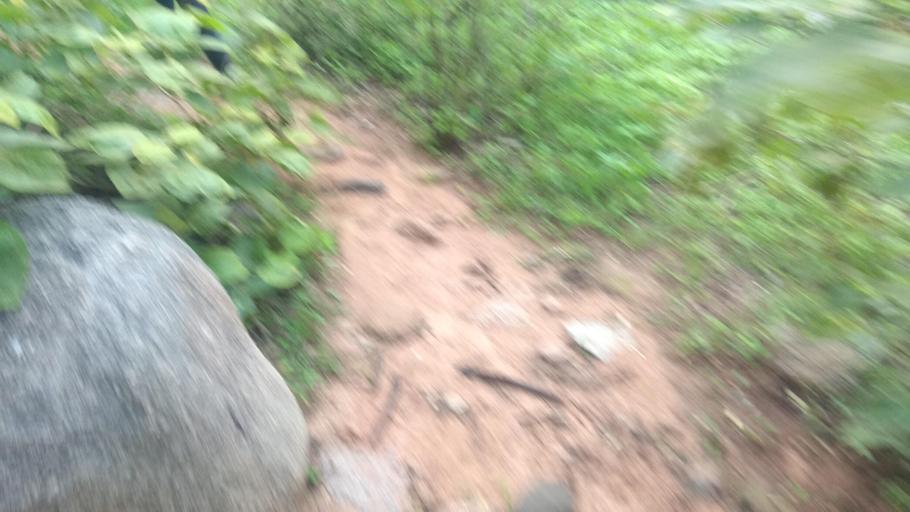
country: IN
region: Telangana
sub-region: Mahbubnagar
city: Farrukhnagar
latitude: 16.8968
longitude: 78.4948
